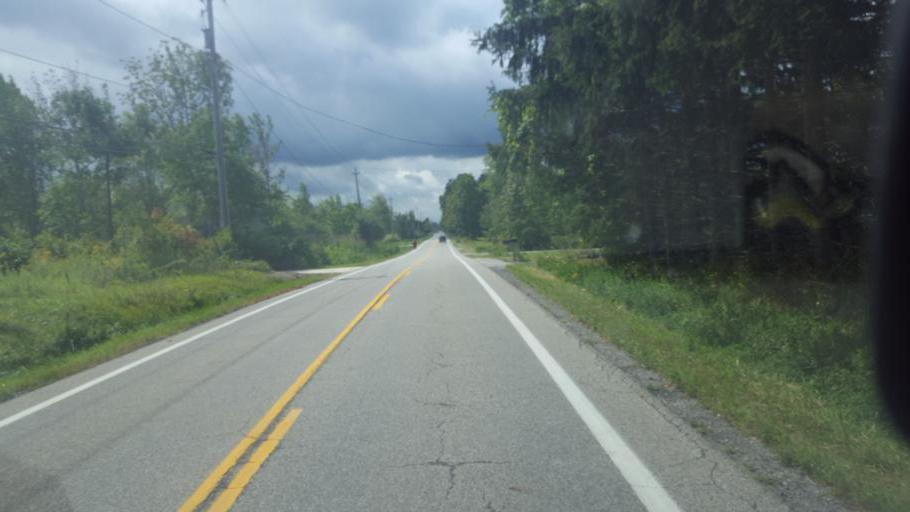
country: US
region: Ohio
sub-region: Geauga County
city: Chardon
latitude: 41.6176
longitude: -81.1302
